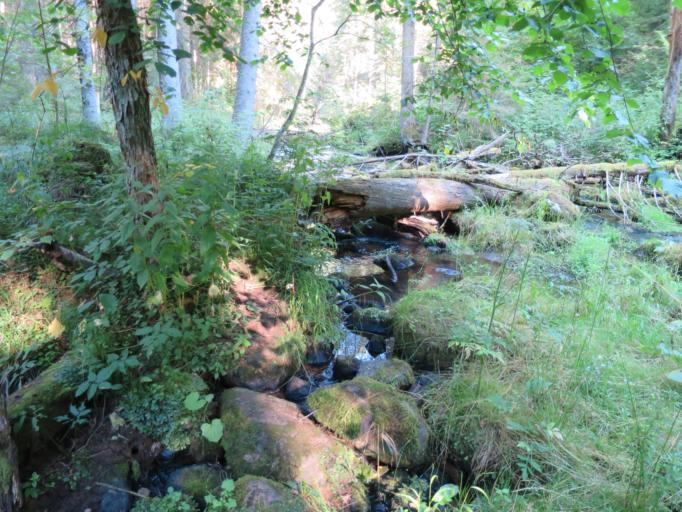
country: LV
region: Ligatne
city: Ligatne
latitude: 57.1292
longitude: 25.1570
